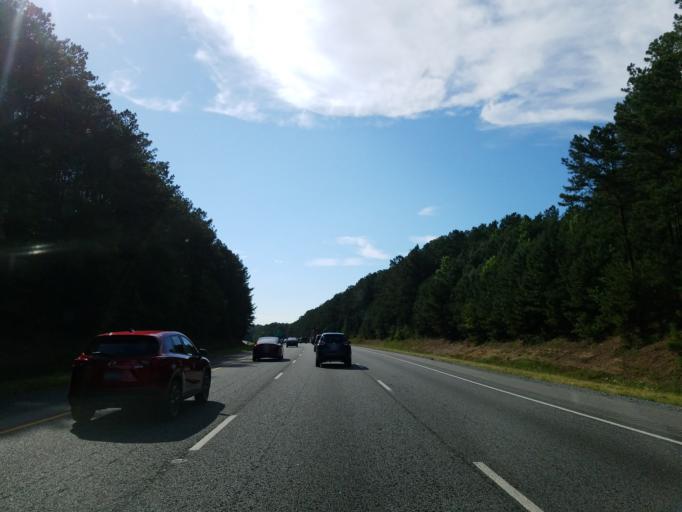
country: US
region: Georgia
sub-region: Bartow County
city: Cartersville
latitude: 34.2414
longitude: -84.7644
